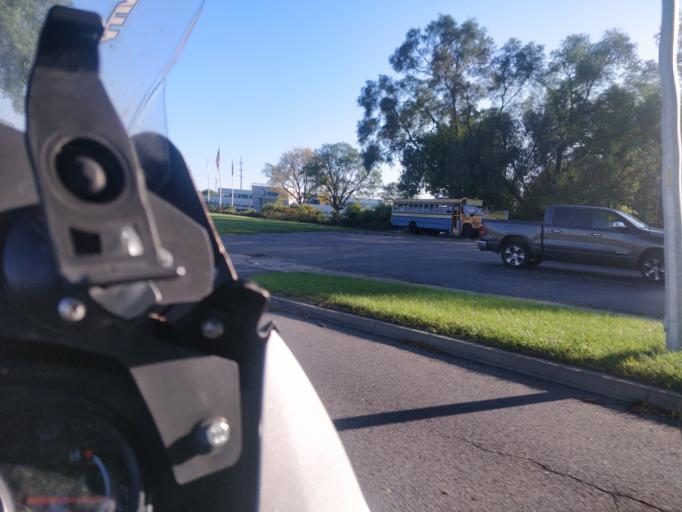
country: US
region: Michigan
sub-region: Wayne County
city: Melvindale
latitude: 42.2675
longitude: -83.1778
